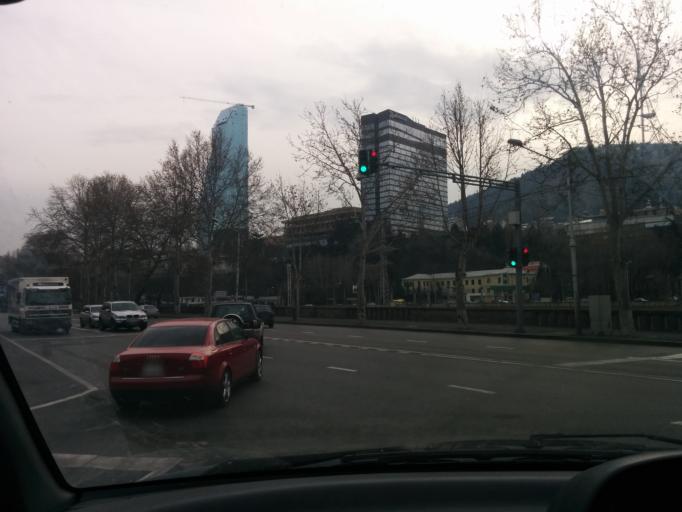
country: GE
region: T'bilisi
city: Tbilisi
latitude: 41.7072
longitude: 44.7941
